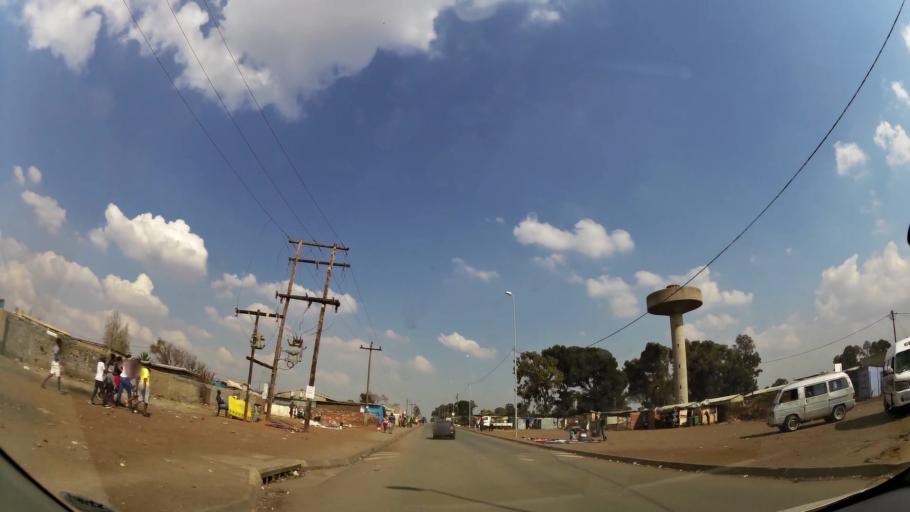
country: ZA
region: Gauteng
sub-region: Ekurhuleni Metropolitan Municipality
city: Germiston
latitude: -26.3143
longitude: 28.1457
